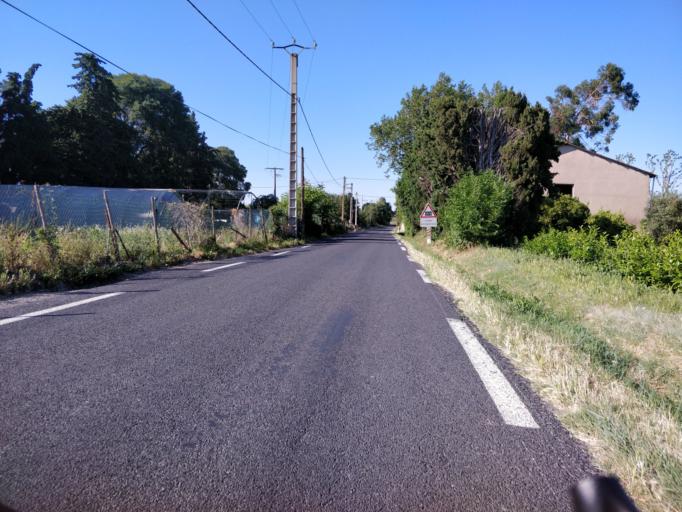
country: FR
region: Languedoc-Roussillon
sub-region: Departement des Pyrenees-Orientales
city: Corneilla-del-Vercol
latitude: 42.6121
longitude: 2.9571
